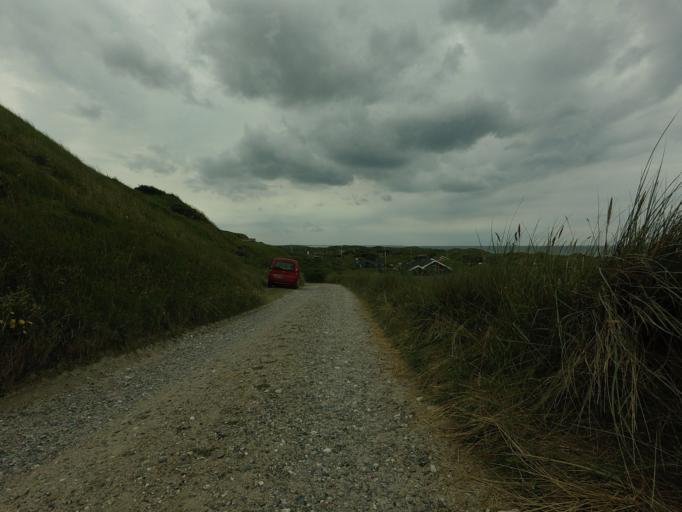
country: DK
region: North Denmark
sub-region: Jammerbugt Kommune
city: Pandrup
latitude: 57.3115
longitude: 9.6514
